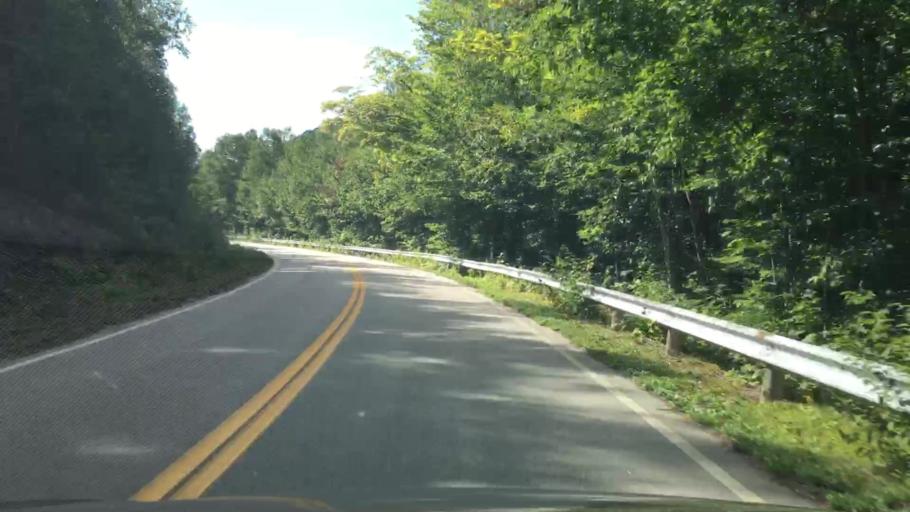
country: US
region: New Hampshire
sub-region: Carroll County
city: North Conway
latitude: 44.0456
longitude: -71.3067
